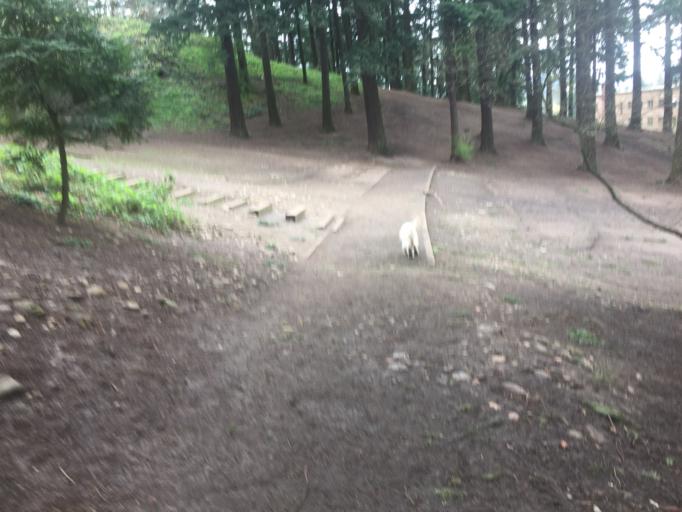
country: US
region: Oregon
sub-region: Multnomah County
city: Lents
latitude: 45.5076
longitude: -122.5940
